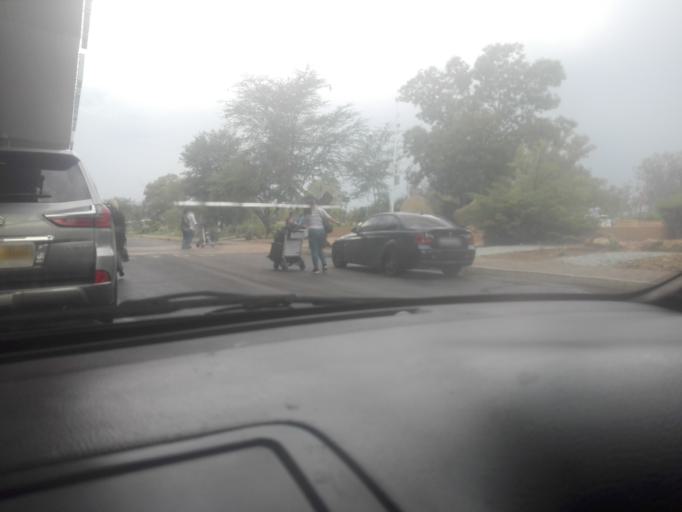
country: BW
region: Kweneng
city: Mmopone
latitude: -24.5581
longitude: 25.9243
